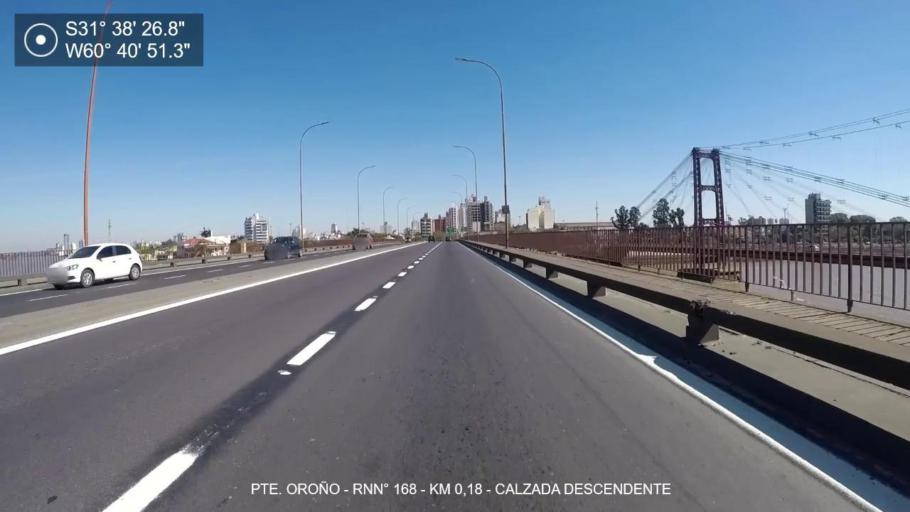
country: AR
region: Santa Fe
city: Santa Fe de la Vera Cruz
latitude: -31.6408
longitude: -60.6810
